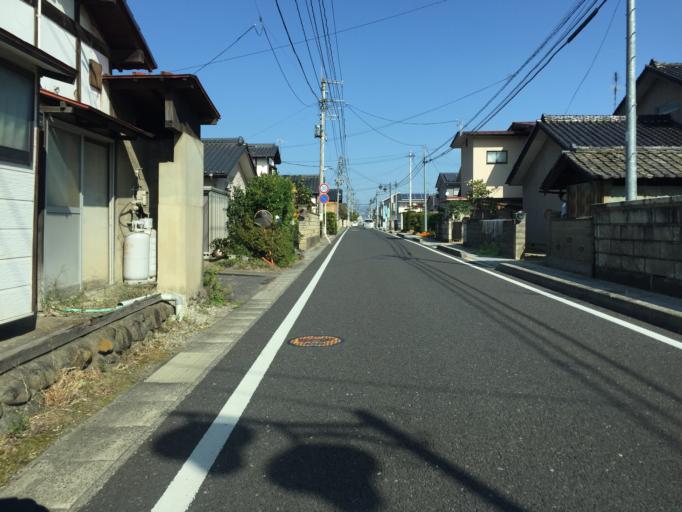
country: JP
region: Fukushima
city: Fukushima-shi
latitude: 37.7245
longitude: 140.4383
